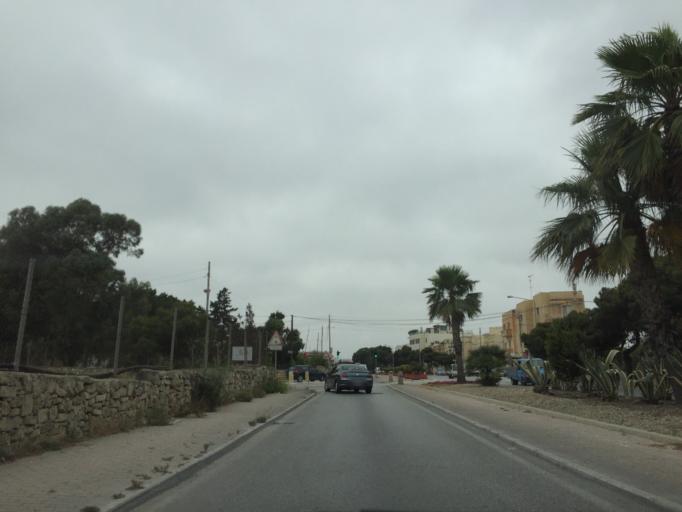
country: MT
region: Attard
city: Attard
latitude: 35.8877
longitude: 14.4335
